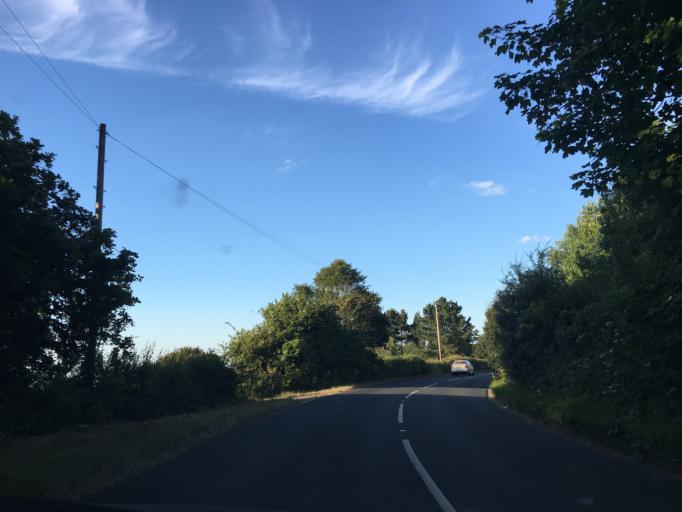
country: GB
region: England
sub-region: Isle of Wight
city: Newport
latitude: 50.7036
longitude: -1.2660
